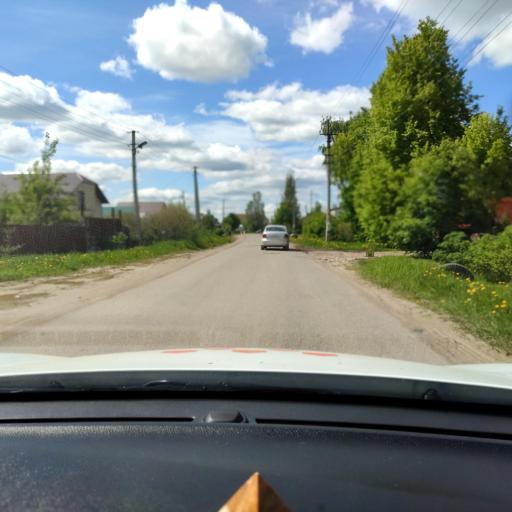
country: RU
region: Tatarstan
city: Osinovo
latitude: 55.8817
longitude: 48.8717
